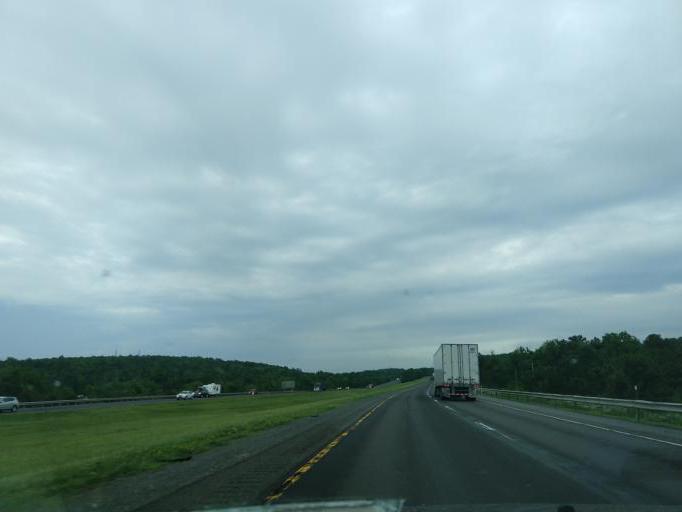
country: US
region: Pennsylvania
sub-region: Luzerne County
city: West Hazleton
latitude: 40.9639
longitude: -76.0282
